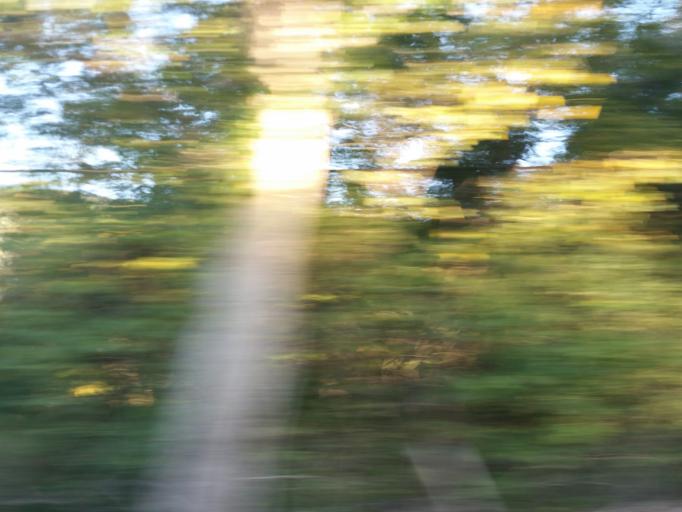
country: US
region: Tennessee
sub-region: Grainger County
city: Rutledge
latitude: 36.3252
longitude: -83.5190
